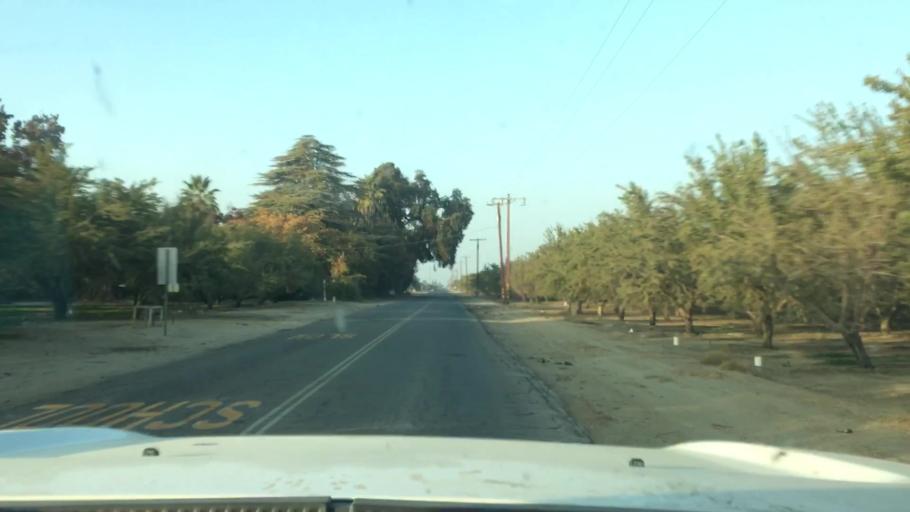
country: US
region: California
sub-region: Kern County
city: Shafter
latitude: 35.4863
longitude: -119.2963
